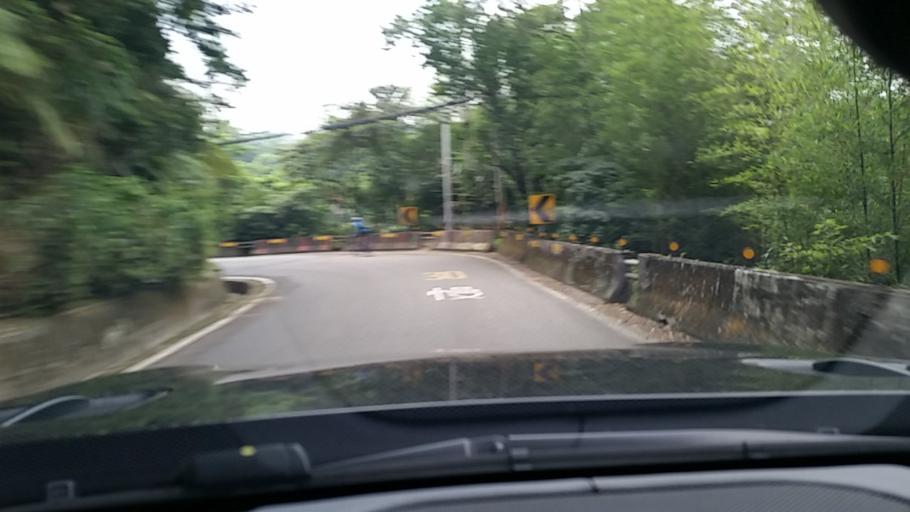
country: TW
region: Taiwan
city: Daxi
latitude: 24.7952
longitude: 121.2800
